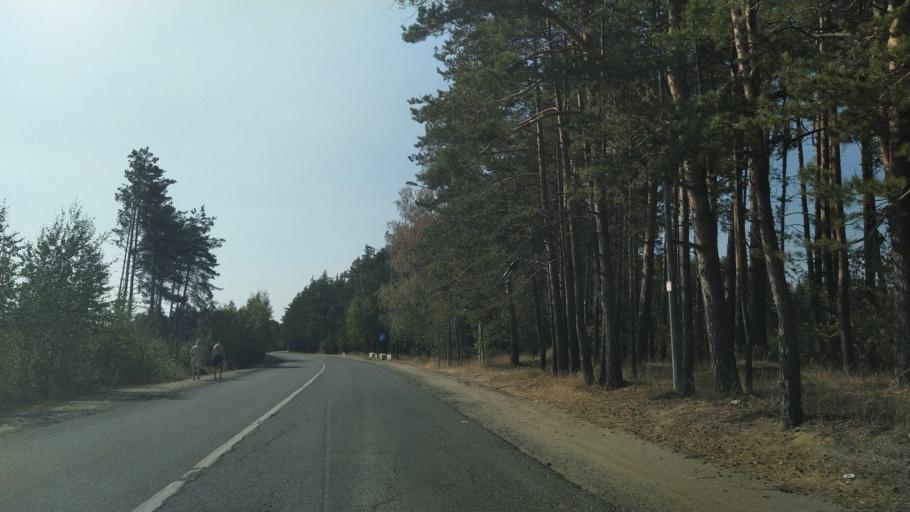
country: RU
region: St.-Petersburg
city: Kolomyagi
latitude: 60.0453
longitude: 30.2594
